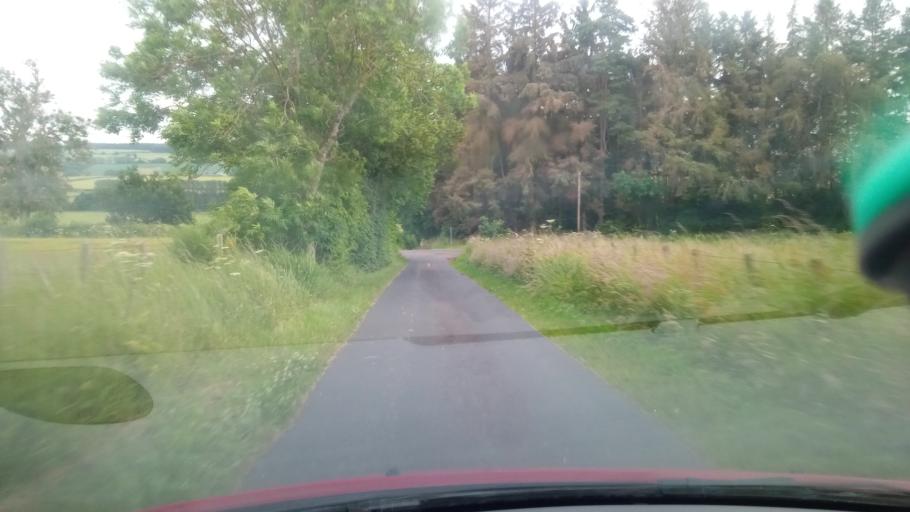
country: GB
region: Scotland
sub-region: The Scottish Borders
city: Jedburgh
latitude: 55.4988
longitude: -2.6195
